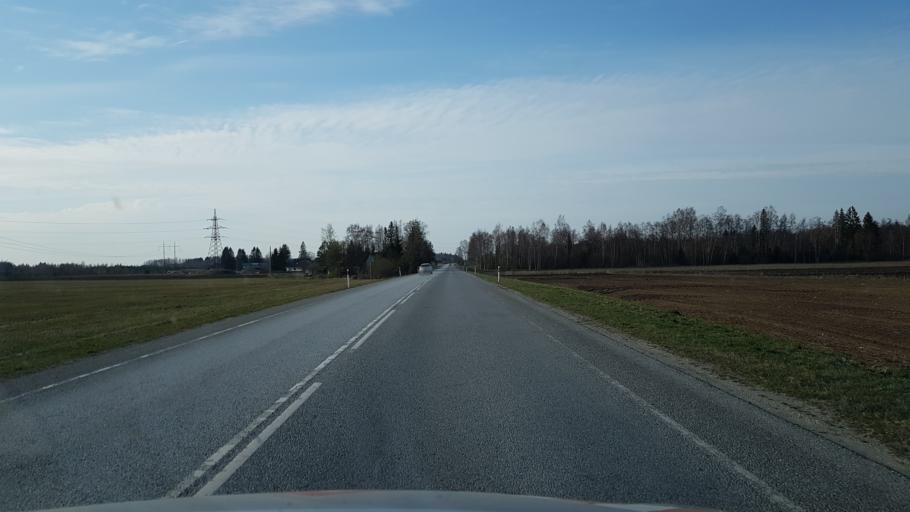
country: EE
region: Laeaene-Virumaa
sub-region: Rakvere linn
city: Rakvere
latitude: 59.3830
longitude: 26.3189
